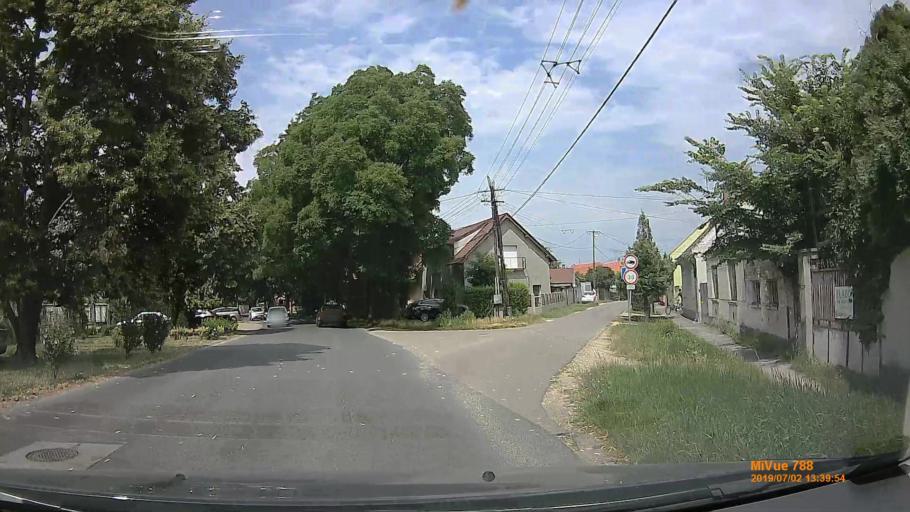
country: HU
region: Gyor-Moson-Sopron
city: Mosonmagyarovar
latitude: 47.8576
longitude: 17.2797
